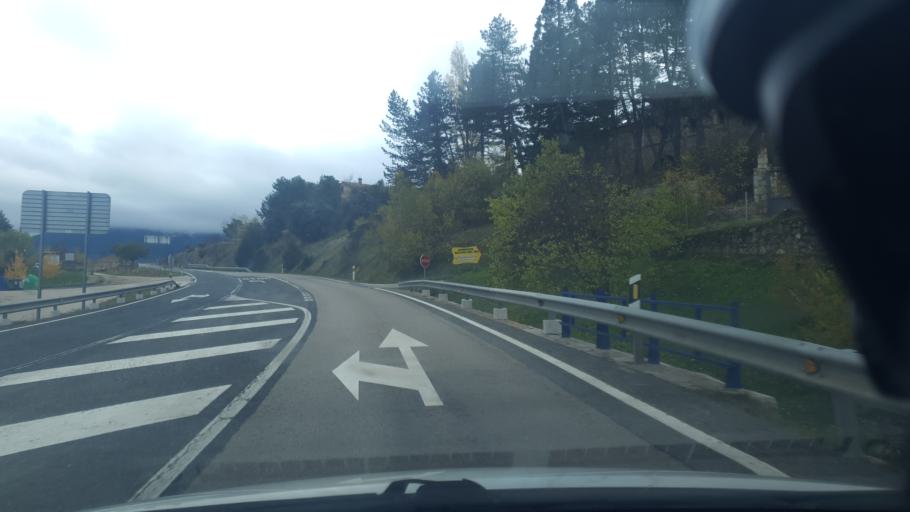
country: ES
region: Castille and Leon
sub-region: Provincia de Segovia
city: Cerezo de Abajo
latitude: 41.2172
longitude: -3.5903
